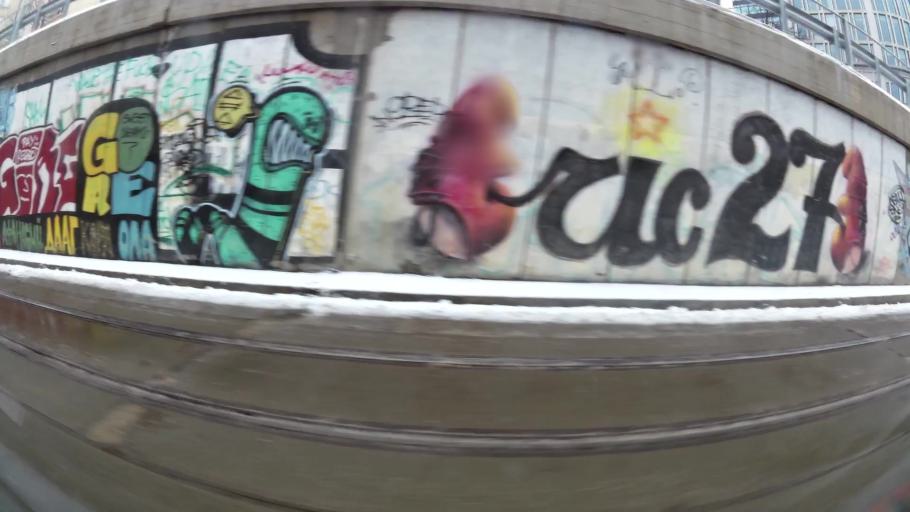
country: BG
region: Sofia-Capital
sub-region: Stolichna Obshtina
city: Sofia
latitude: 42.6848
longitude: 23.3210
